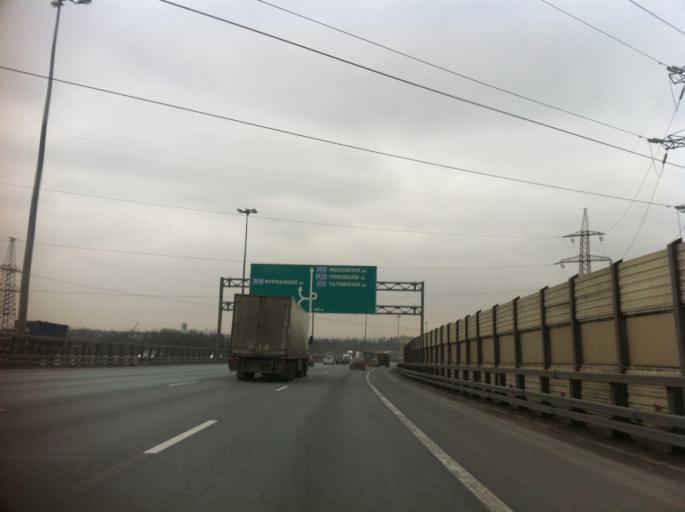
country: RU
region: St.-Petersburg
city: Obukhovo
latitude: 59.8274
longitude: 30.4375
